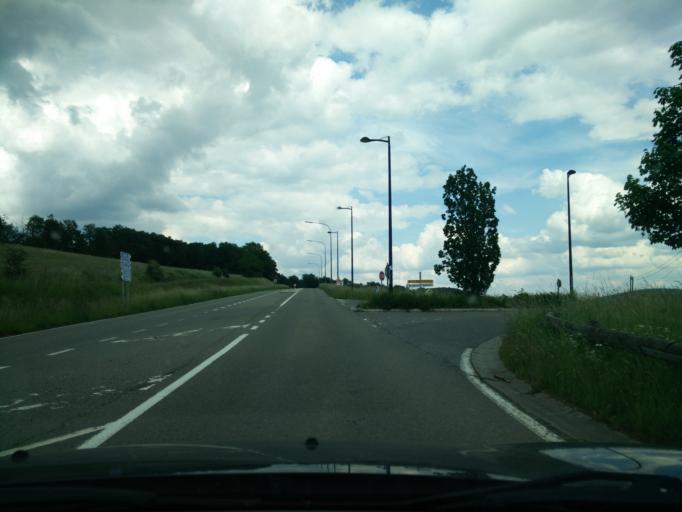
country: FR
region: Champagne-Ardenne
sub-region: Departement des Ardennes
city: Vireux-Molhain
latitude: 50.0787
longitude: 4.6233
